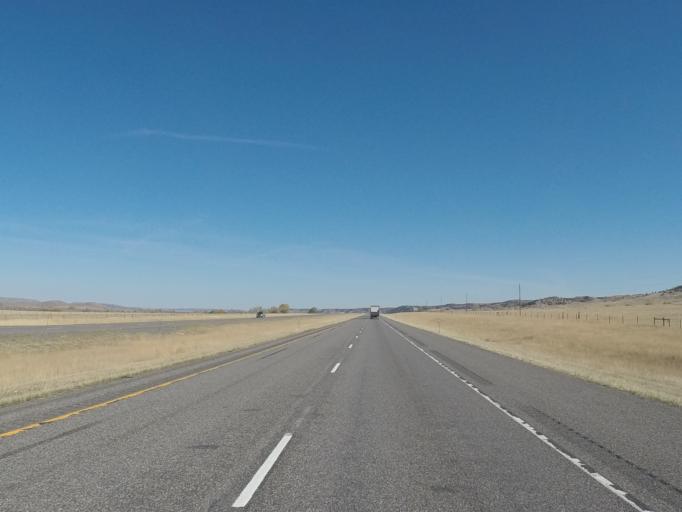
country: US
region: Montana
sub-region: Sweet Grass County
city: Big Timber
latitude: 45.7486
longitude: -110.1689
